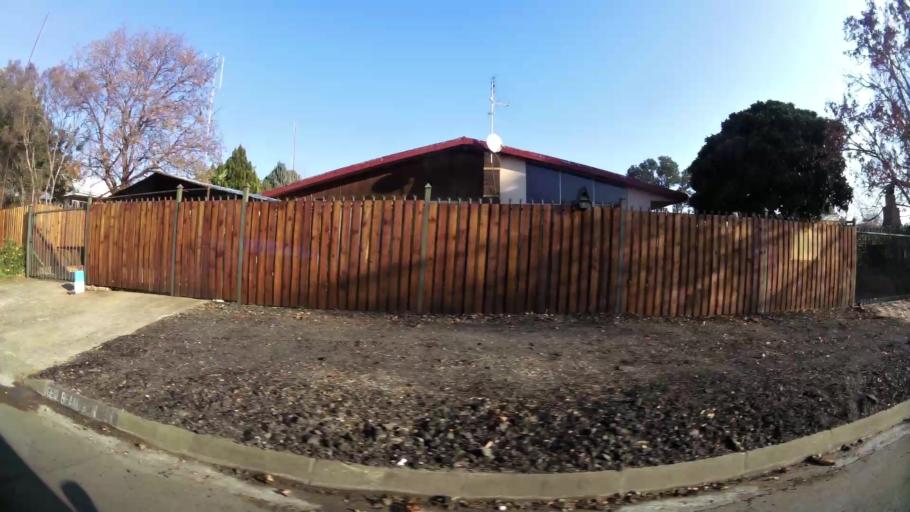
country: ZA
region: Orange Free State
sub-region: Mangaung Metropolitan Municipality
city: Bloemfontein
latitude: -29.1512
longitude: 26.2002
